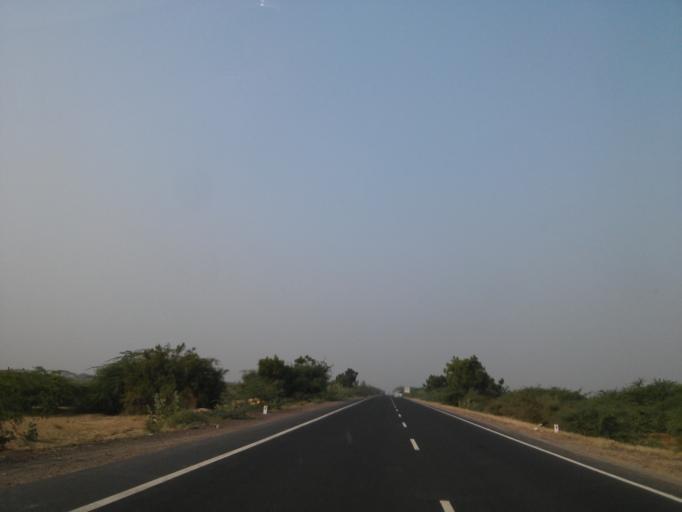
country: IN
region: Gujarat
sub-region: Kachchh
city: Anjar
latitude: 23.2898
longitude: 70.0232
